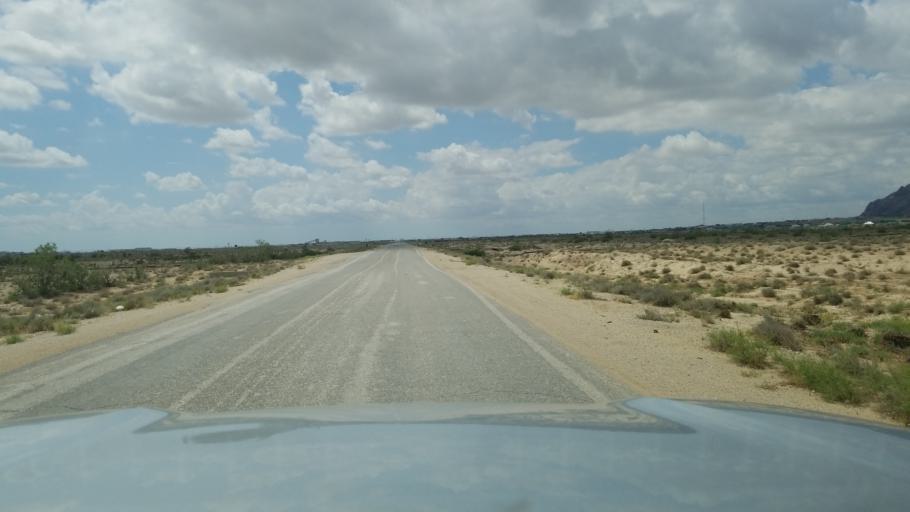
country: TM
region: Balkan
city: Balkanabat
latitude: 39.4864
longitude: 54.4190
